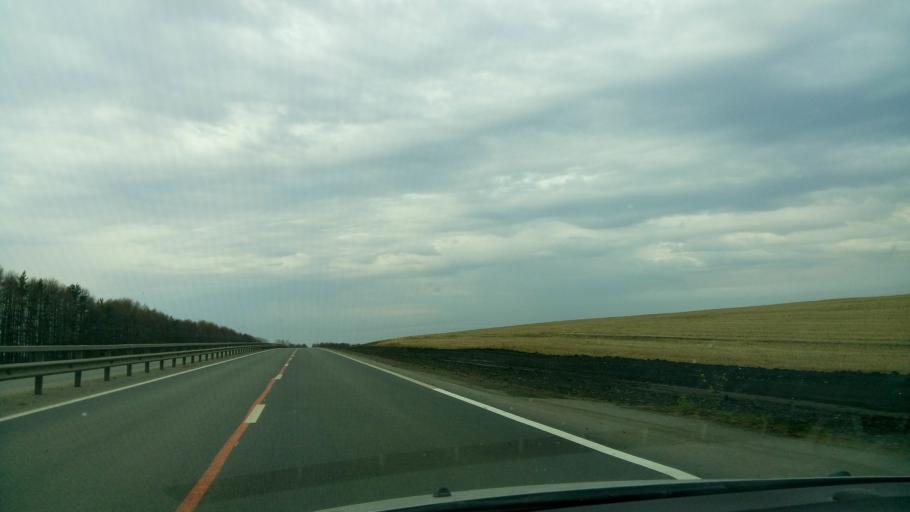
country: RU
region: Sverdlovsk
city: Kamyshlov
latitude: 56.8548
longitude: 62.8785
